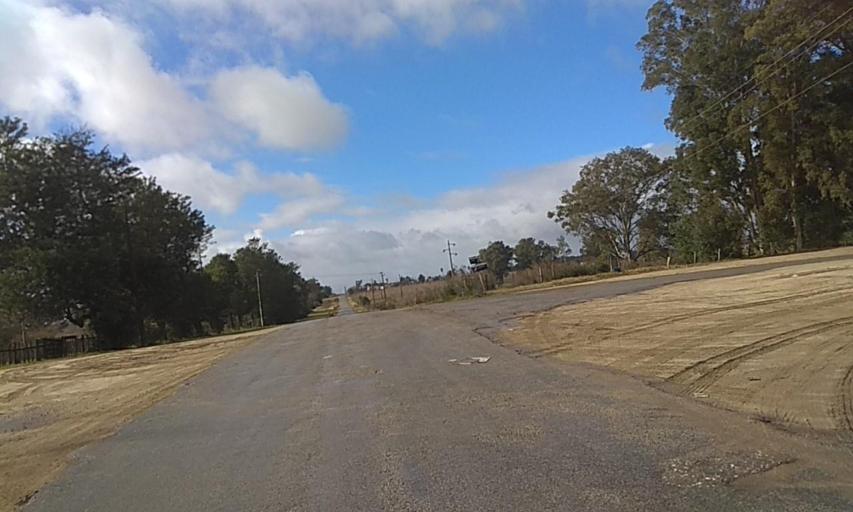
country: UY
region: Florida
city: Florida
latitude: -34.0934
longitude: -56.1964
